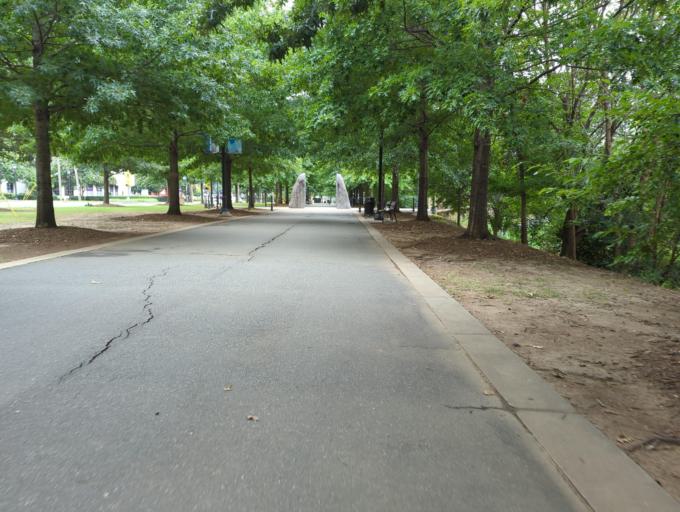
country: US
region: North Carolina
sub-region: Mecklenburg County
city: Charlotte
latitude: 35.2076
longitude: -80.8361
